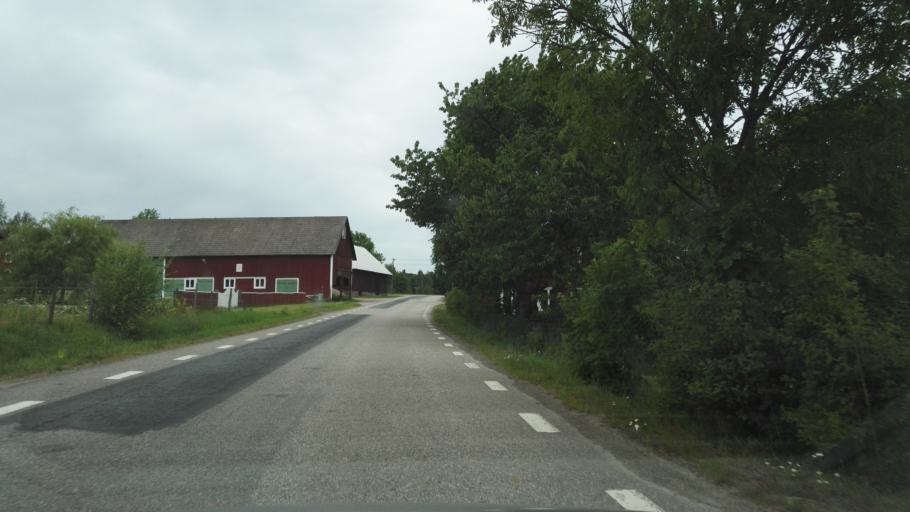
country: SE
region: Kronoberg
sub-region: Vaxjo Kommun
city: Braas
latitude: 57.1113
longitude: 14.9782
